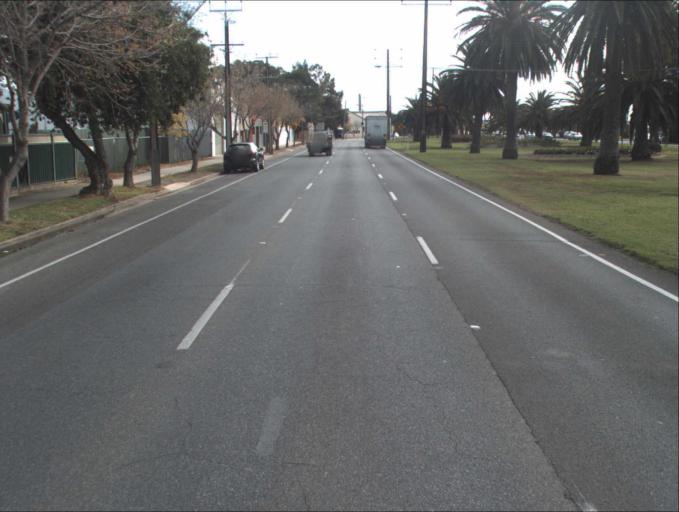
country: AU
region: South Australia
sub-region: Port Adelaide Enfield
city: Alberton
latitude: -34.8559
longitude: 138.5103
